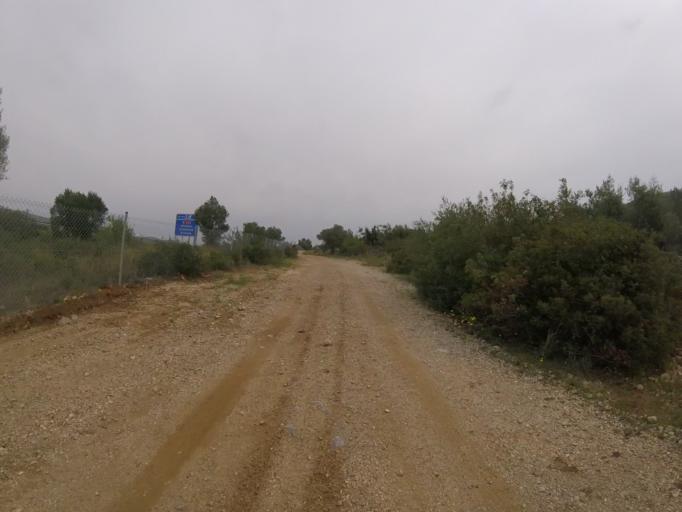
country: ES
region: Valencia
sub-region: Provincia de Castello
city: Santa Magdalena de Pulpis
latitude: 40.3668
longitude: 0.3290
